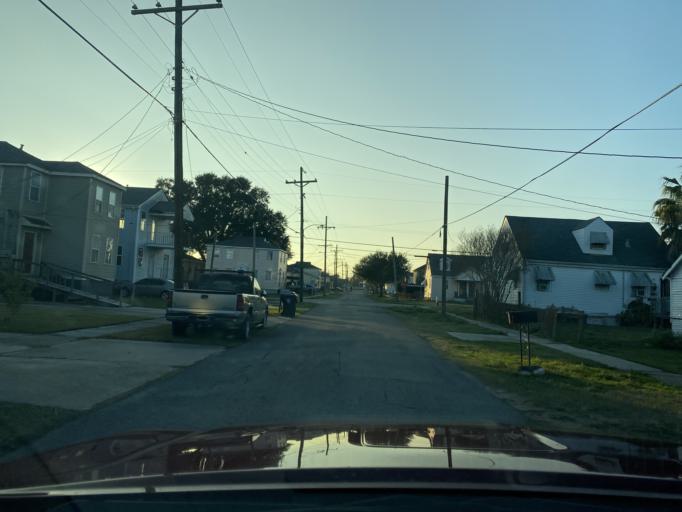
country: US
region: Louisiana
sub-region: Orleans Parish
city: New Orleans
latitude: 30.0211
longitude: -90.0580
